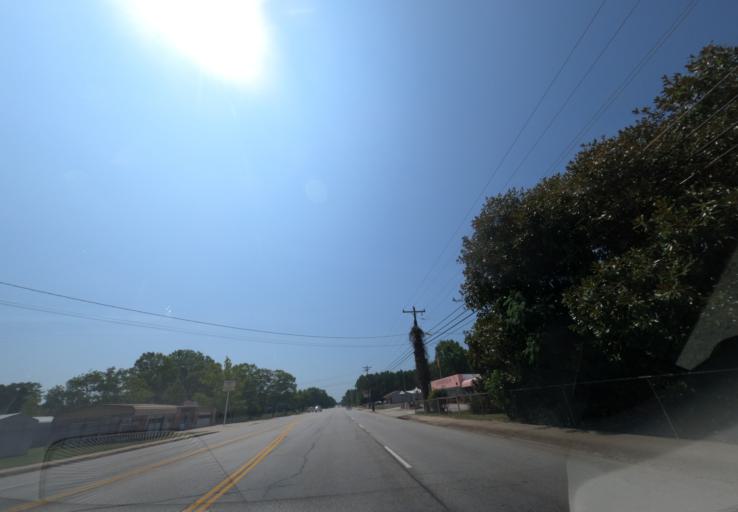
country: US
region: South Carolina
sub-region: Greenwood County
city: Greenwood
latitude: 34.1489
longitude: -82.1367
